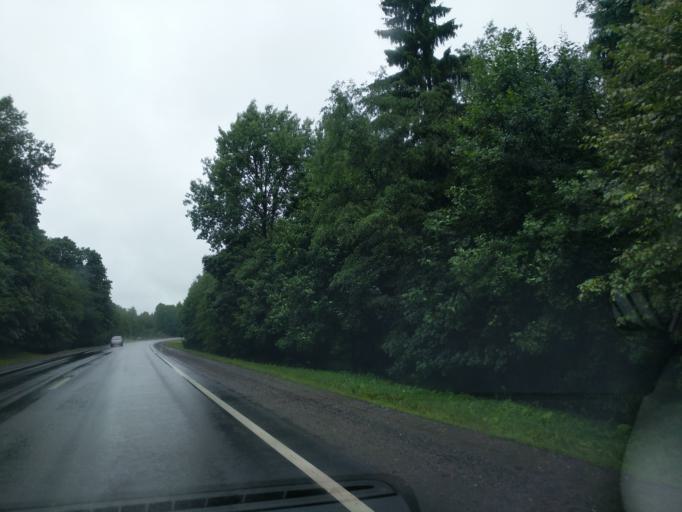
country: BY
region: Minsk
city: Syomkava
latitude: 54.1468
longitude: 27.5066
